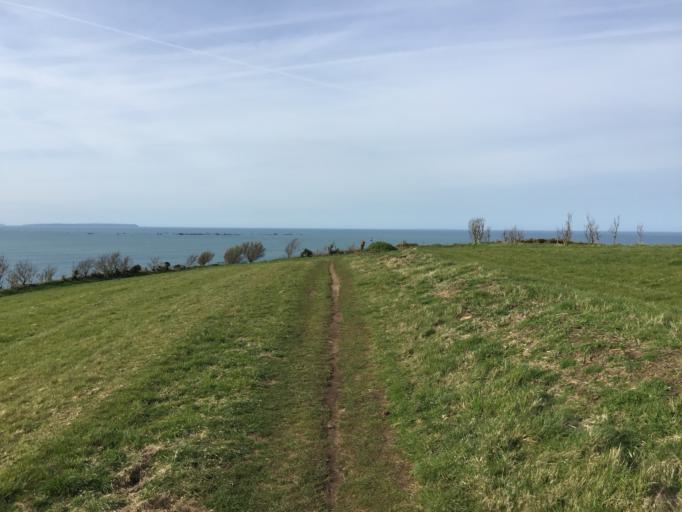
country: JE
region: St Helier
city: Saint Helier
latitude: 49.2502
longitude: -2.1724
